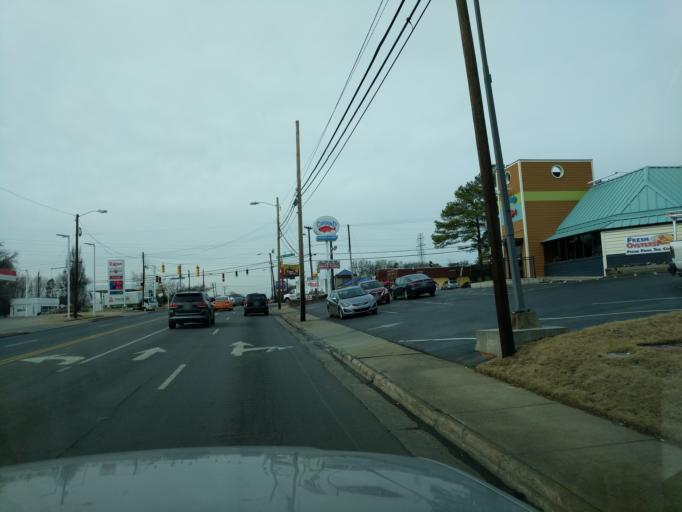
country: US
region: North Carolina
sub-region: Mecklenburg County
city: Charlotte
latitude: 35.1789
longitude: -80.8825
